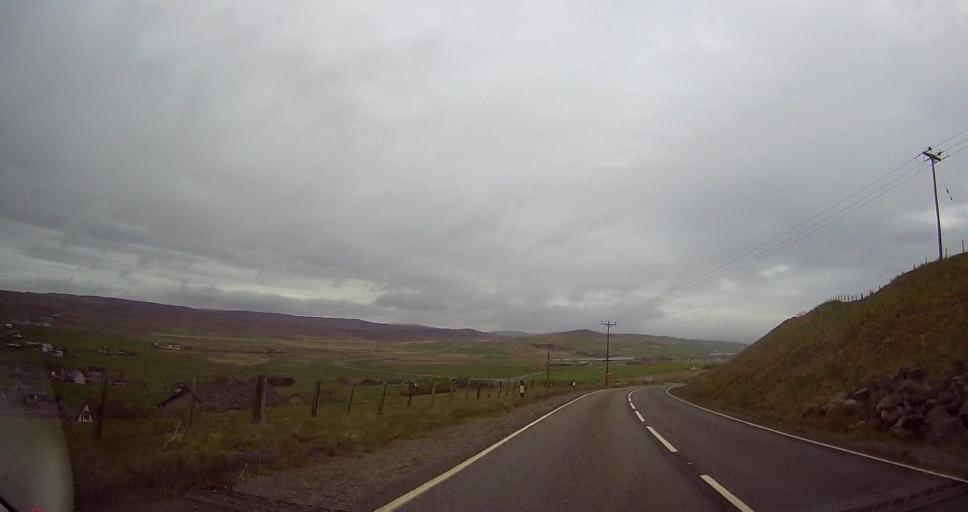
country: GB
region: Scotland
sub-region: Shetland Islands
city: Lerwick
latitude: 60.1808
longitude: -1.2249
